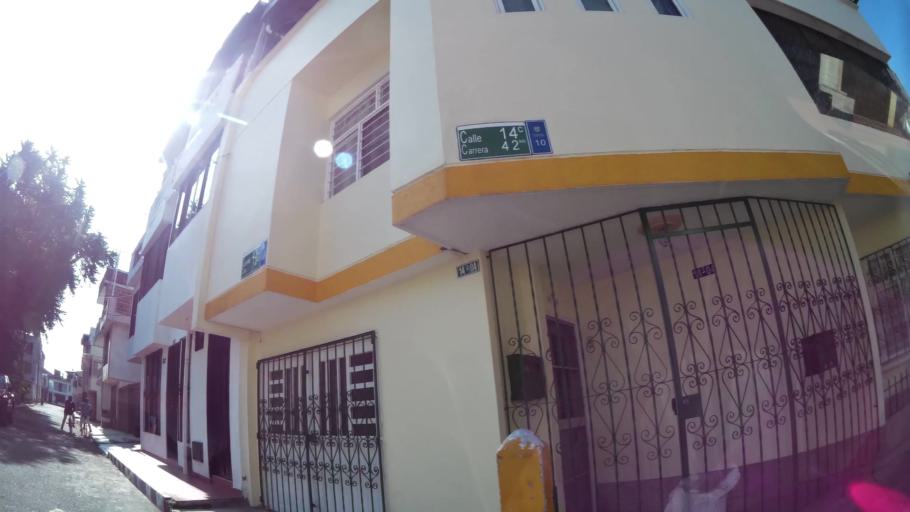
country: CO
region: Valle del Cauca
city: Cali
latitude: 3.4148
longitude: -76.5263
